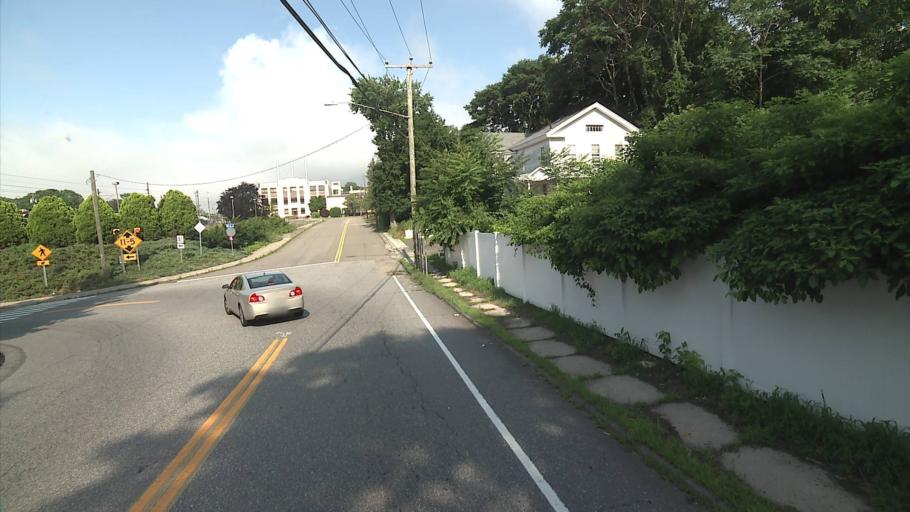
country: US
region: Connecticut
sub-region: Middlesex County
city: Clinton
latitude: 41.2800
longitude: -72.5275
